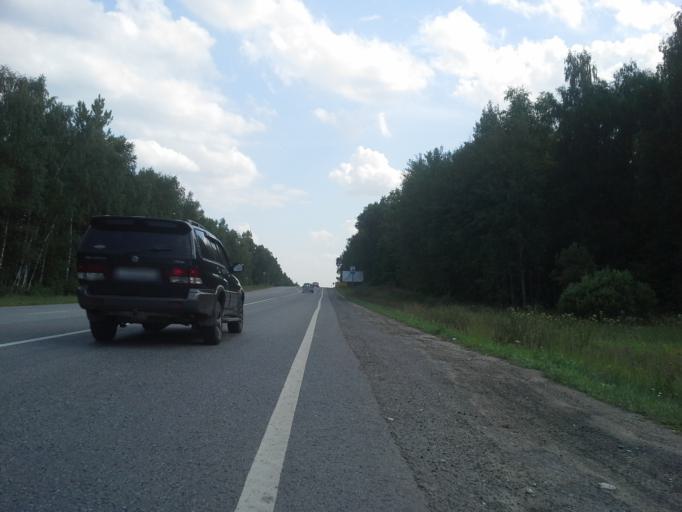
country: RU
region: Moskovskaya
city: Vostryakovo
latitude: 55.3465
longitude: 37.7982
